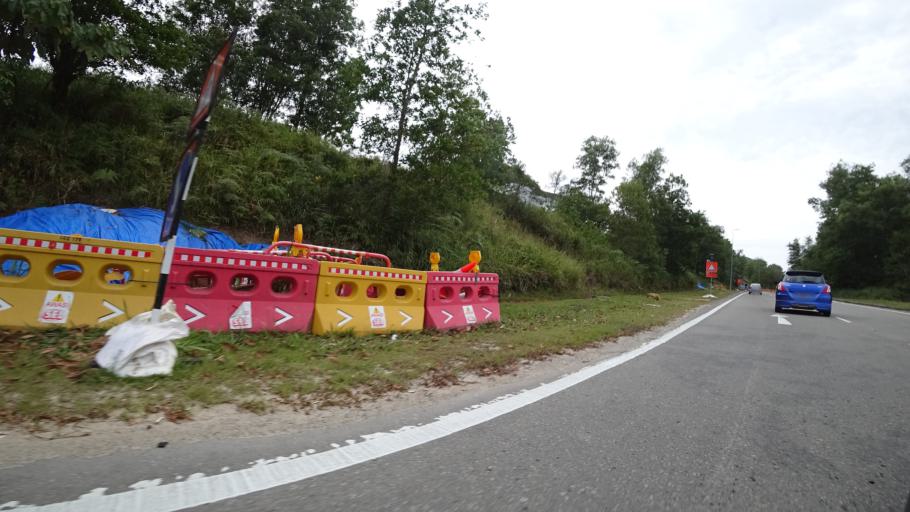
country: BN
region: Brunei and Muara
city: Bandar Seri Begawan
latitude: 4.9007
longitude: 114.8741
